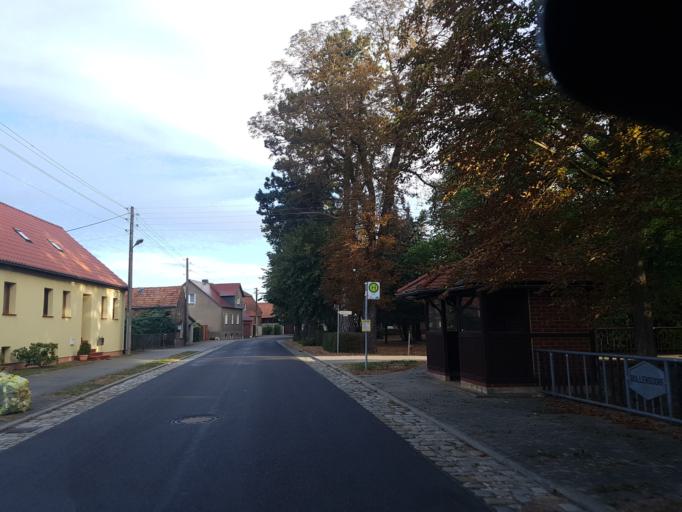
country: DE
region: Brandenburg
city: Dahme
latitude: 51.8319
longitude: 13.3889
